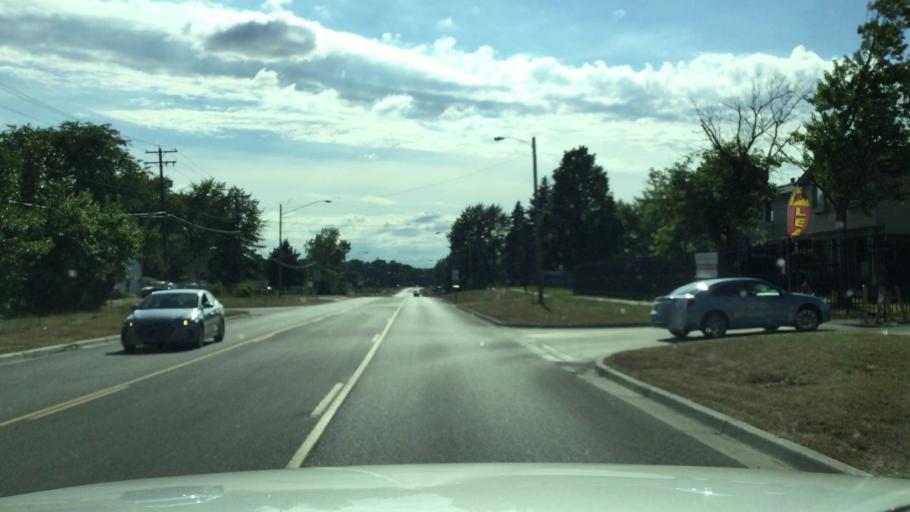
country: US
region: Michigan
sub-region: Genesee County
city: Beecher
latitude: 43.0902
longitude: -83.7155
